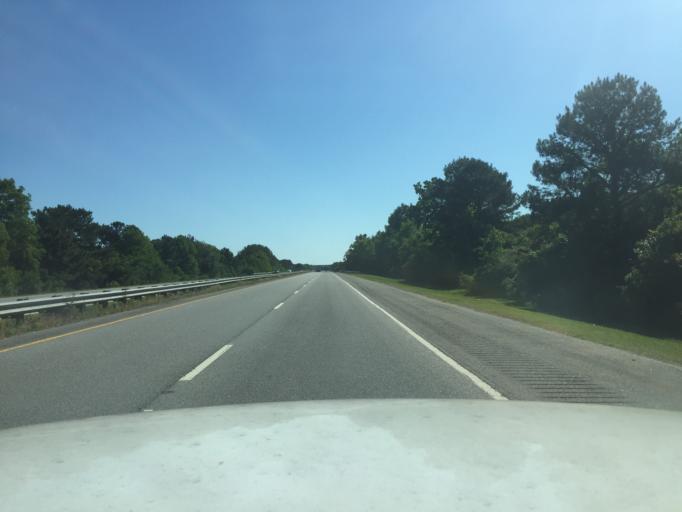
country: US
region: Georgia
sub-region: Chatham County
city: Georgetown
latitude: 32.0050
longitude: -81.1956
